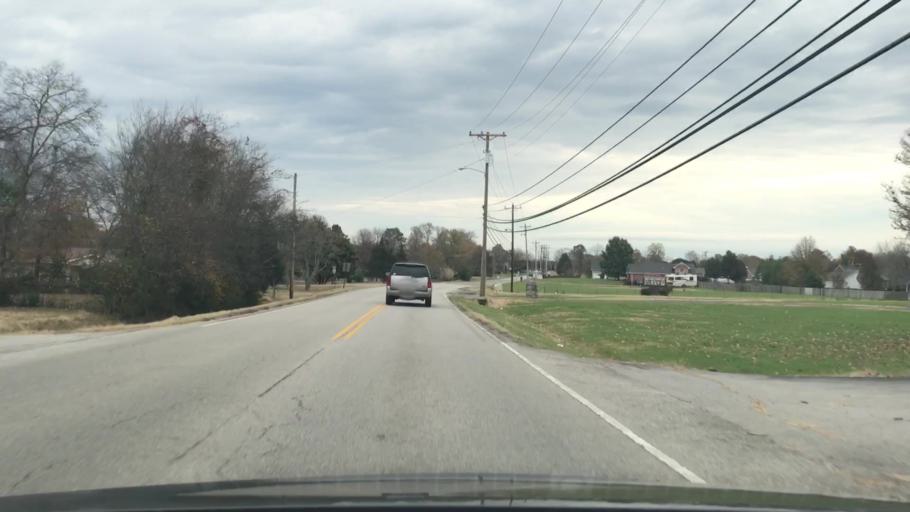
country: US
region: Tennessee
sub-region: Wilson County
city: Lebanon
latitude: 36.2216
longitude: -86.2790
